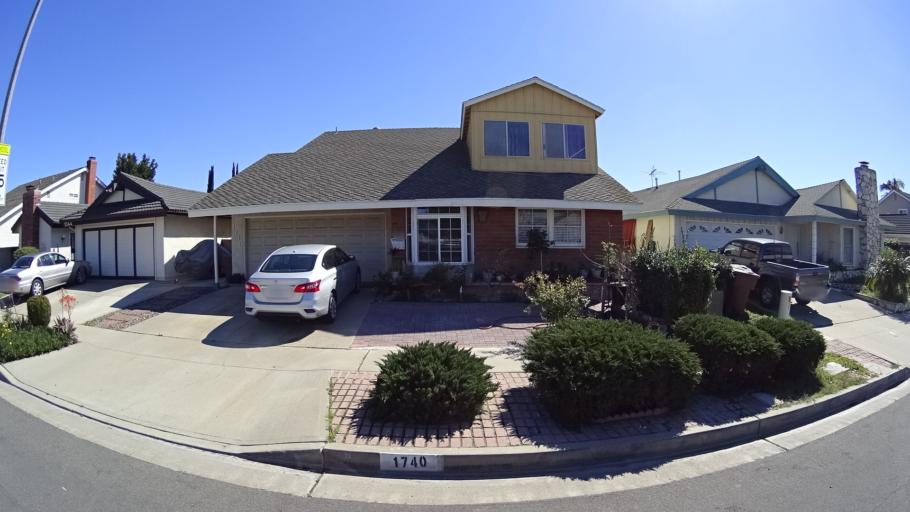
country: US
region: California
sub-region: Orange County
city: Yorba Linda
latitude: 33.8678
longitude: -117.8134
